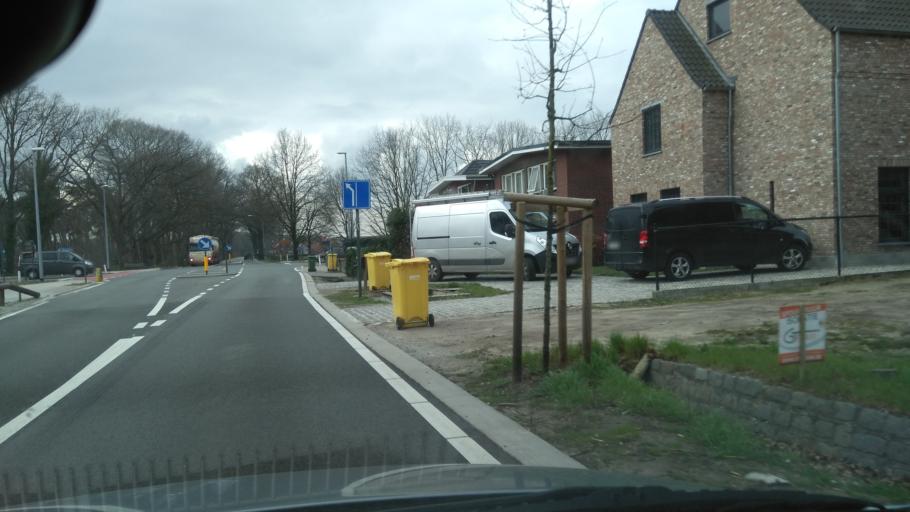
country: BE
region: Flanders
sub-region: Provincie Antwerpen
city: Baarle-Hertog
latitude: 51.3932
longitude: 4.9381
